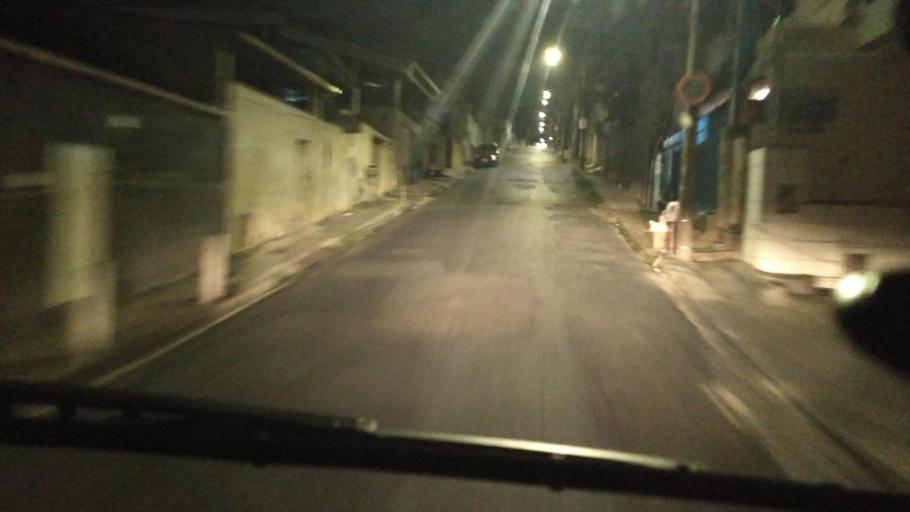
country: BR
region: Minas Gerais
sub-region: Belo Horizonte
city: Belo Horizonte
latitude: -19.8992
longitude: -43.9570
